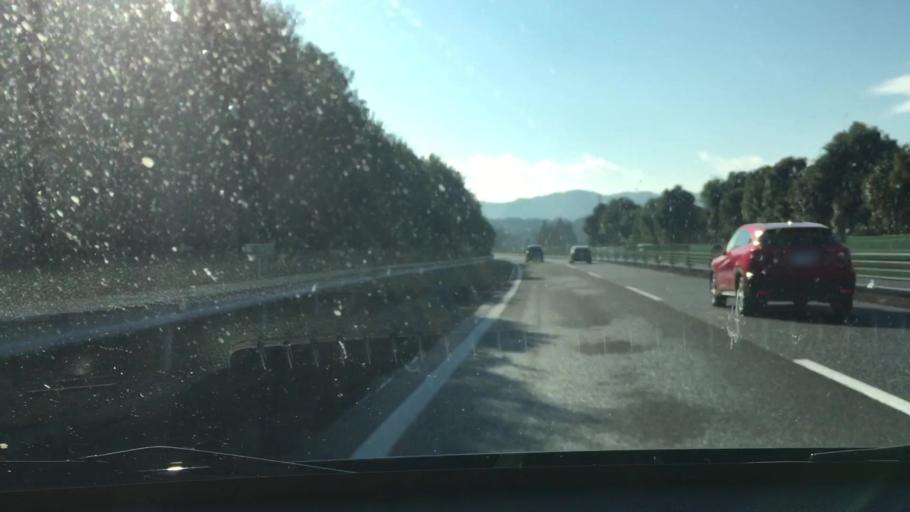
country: JP
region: Kagoshima
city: Okuchi-shinohara
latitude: 32.0148
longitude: 130.7619
